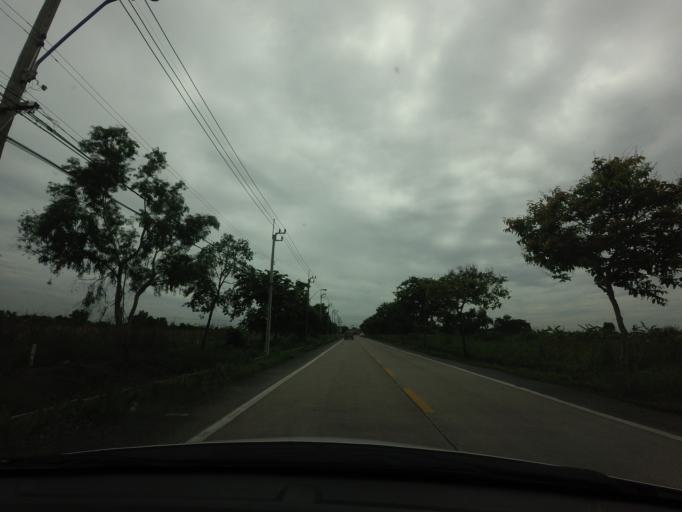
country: TH
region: Pathum Thani
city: Lam Luk Ka
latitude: 13.9191
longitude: 100.7833
